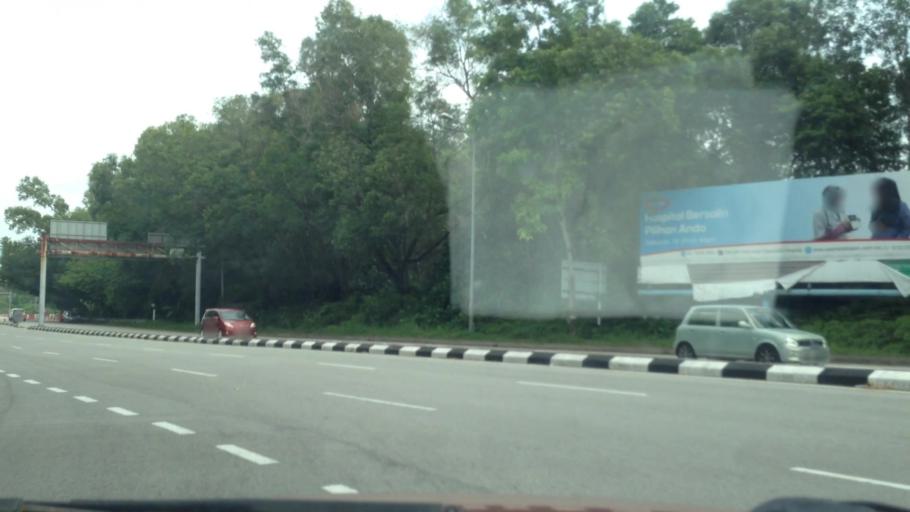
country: MY
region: Selangor
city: Shah Alam
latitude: 3.0808
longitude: 101.5545
